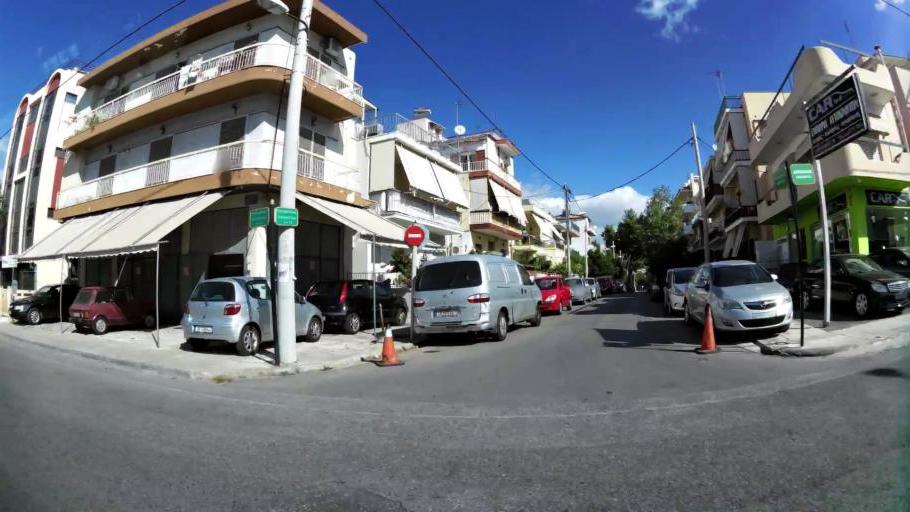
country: GR
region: Attica
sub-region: Nomarchia Athinas
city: Neo Psychiko
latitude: 38.0013
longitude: 23.7865
